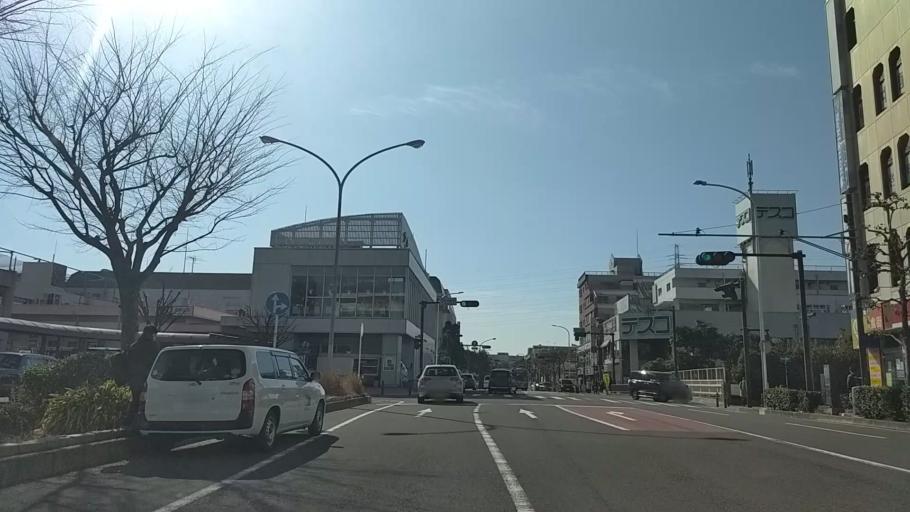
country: JP
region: Kanagawa
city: Kamakura
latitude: 35.3758
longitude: 139.5761
